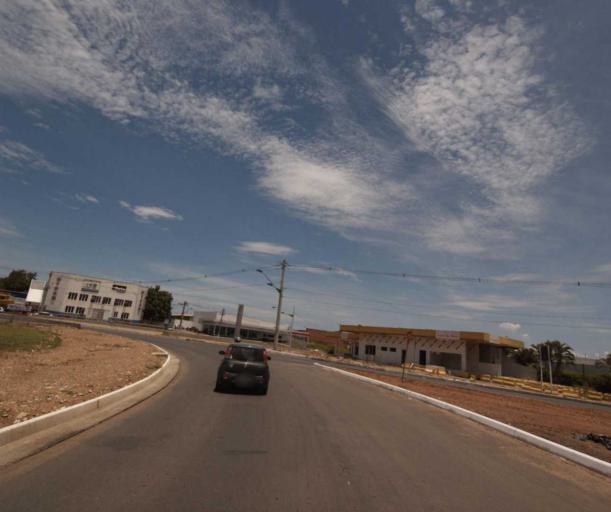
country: BR
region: Mato Grosso
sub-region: Varzea Grande
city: Varzea Grande
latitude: -15.6384
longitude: -56.1200
